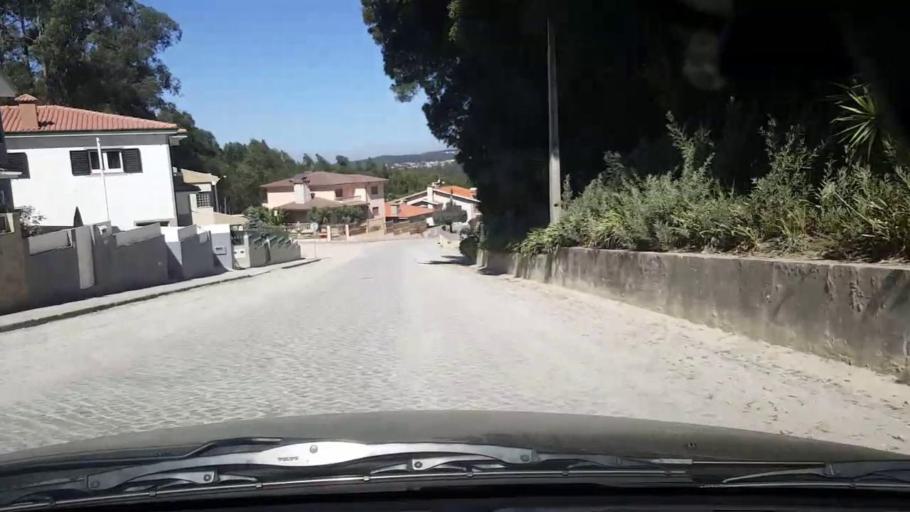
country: PT
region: Porto
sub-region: Maia
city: Gemunde
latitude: 41.3368
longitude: -8.6460
